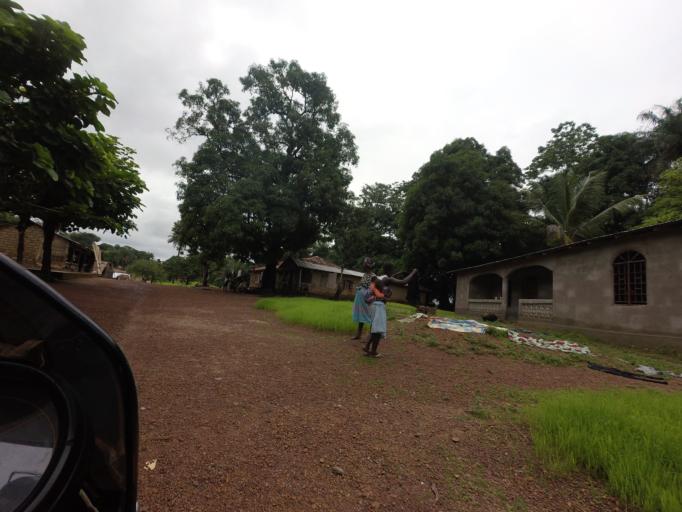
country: SL
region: Northern Province
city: Mambolo
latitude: 8.9700
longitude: -13.0004
